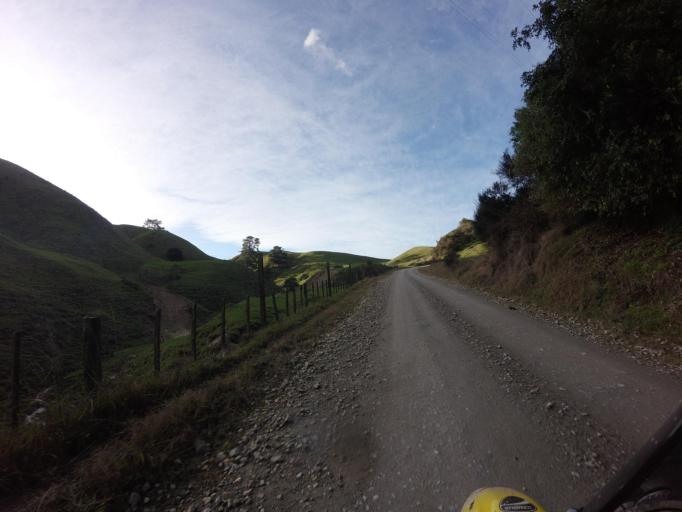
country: NZ
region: Hawke's Bay
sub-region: Wairoa District
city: Wairoa
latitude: -38.7206
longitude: 177.5346
